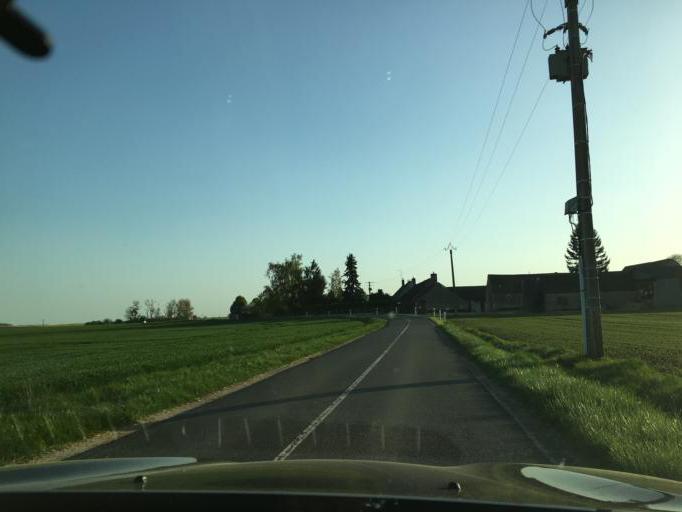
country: FR
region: Centre
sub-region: Departement du Loir-et-Cher
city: Ouzouer-le-Marche
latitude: 47.8587
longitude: 1.5250
